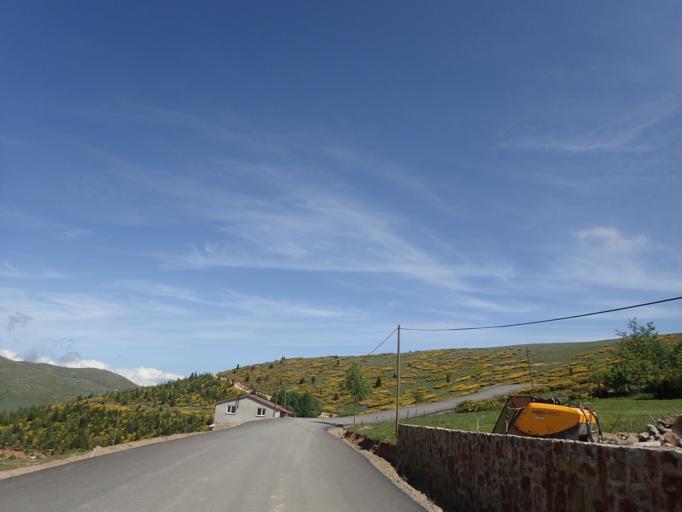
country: TR
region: Ordu
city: Yesilce
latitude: 40.6295
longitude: 37.9553
